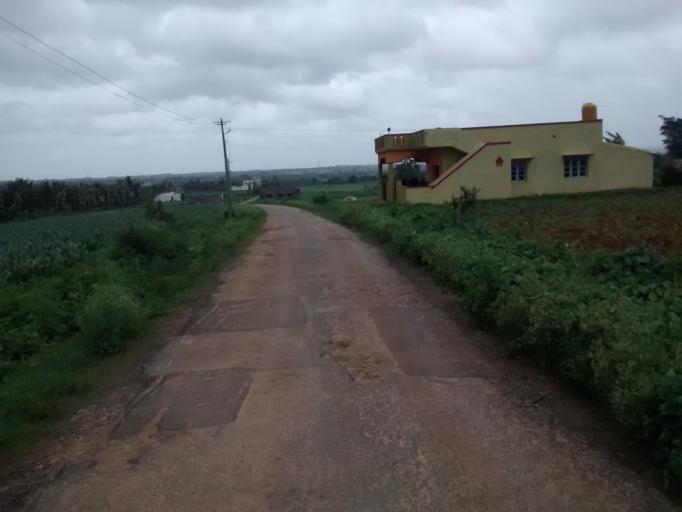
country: IN
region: Karnataka
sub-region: Hassan
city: Hassan
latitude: 12.9477
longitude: 76.1352
